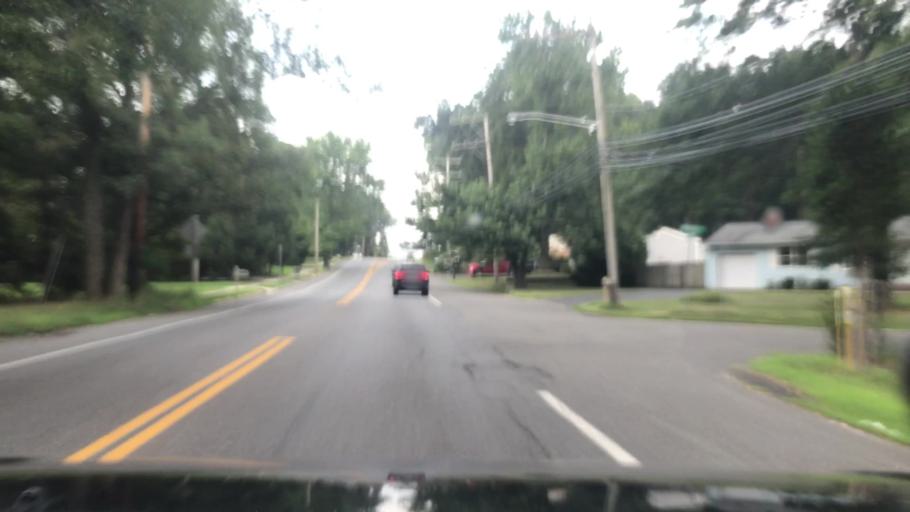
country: US
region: New Jersey
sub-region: Ocean County
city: Lakewood
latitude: 40.0874
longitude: -74.2672
